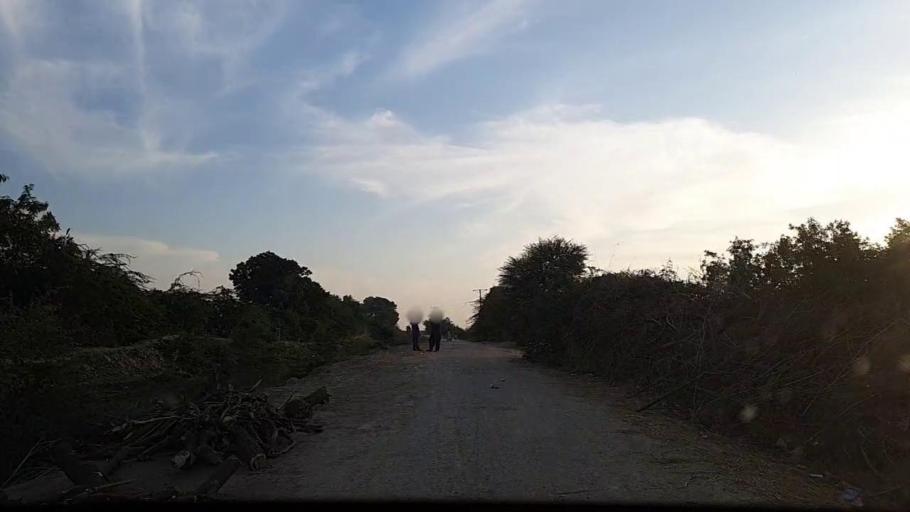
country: PK
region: Sindh
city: Mirpur Batoro
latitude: 24.6373
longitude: 68.1369
